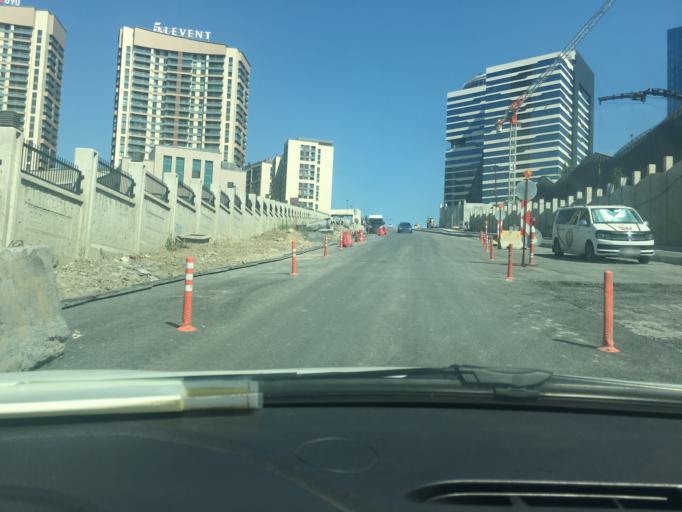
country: TR
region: Istanbul
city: Sisli
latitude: 41.0901
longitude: 28.9526
